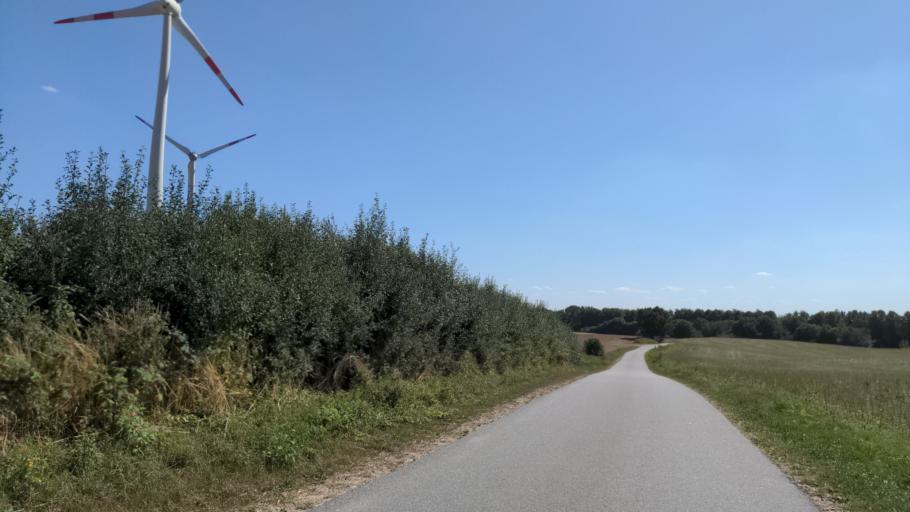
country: DE
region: Mecklenburg-Vorpommern
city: Selmsdorf
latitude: 53.8741
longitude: 10.8952
